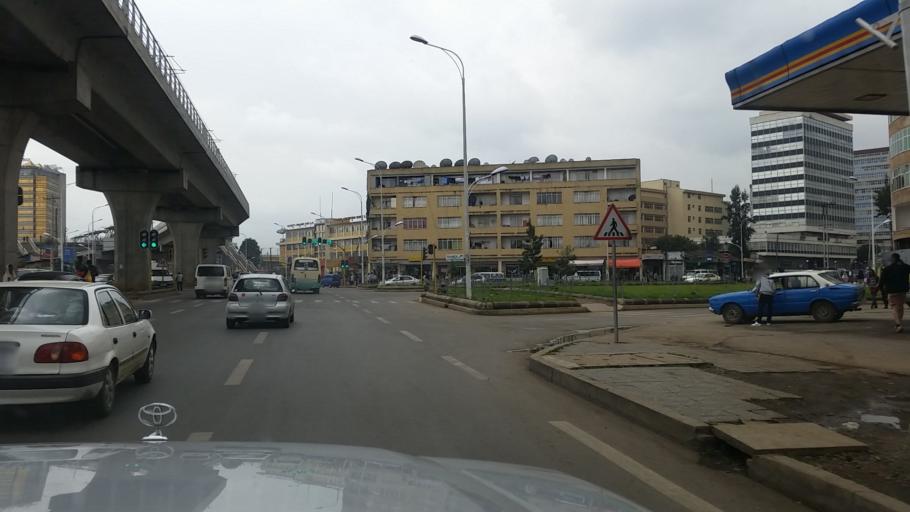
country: ET
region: Adis Abeba
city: Addis Ababa
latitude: 9.0116
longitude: 38.7506
